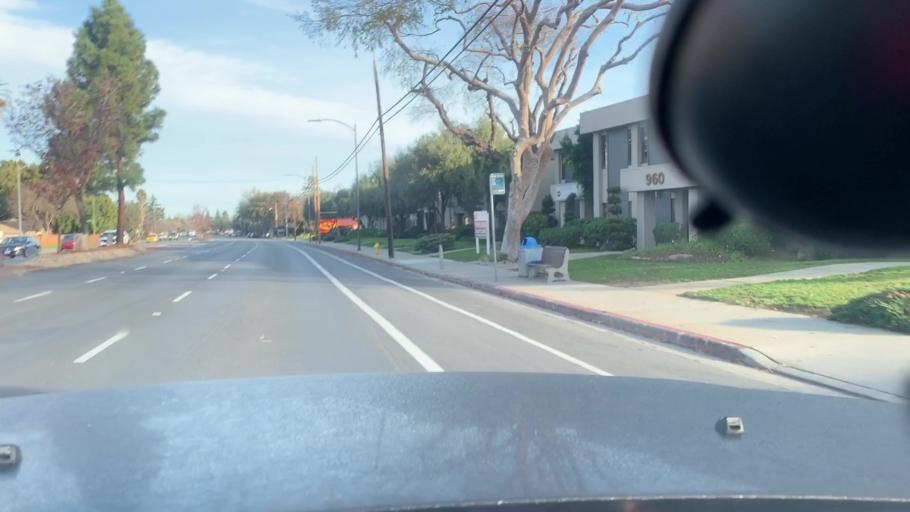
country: US
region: California
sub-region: Santa Clara County
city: Campbell
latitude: 37.3088
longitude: -121.9774
